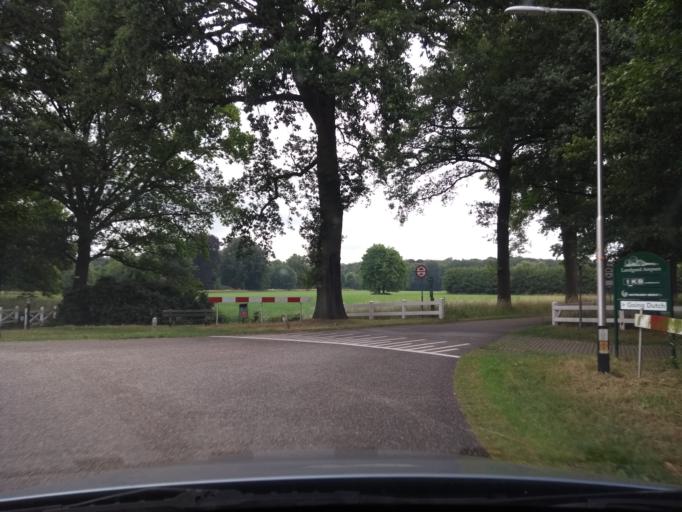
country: NL
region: Gelderland
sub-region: Gemeente Lochem
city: Lochem
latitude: 52.1689
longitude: 6.4233
